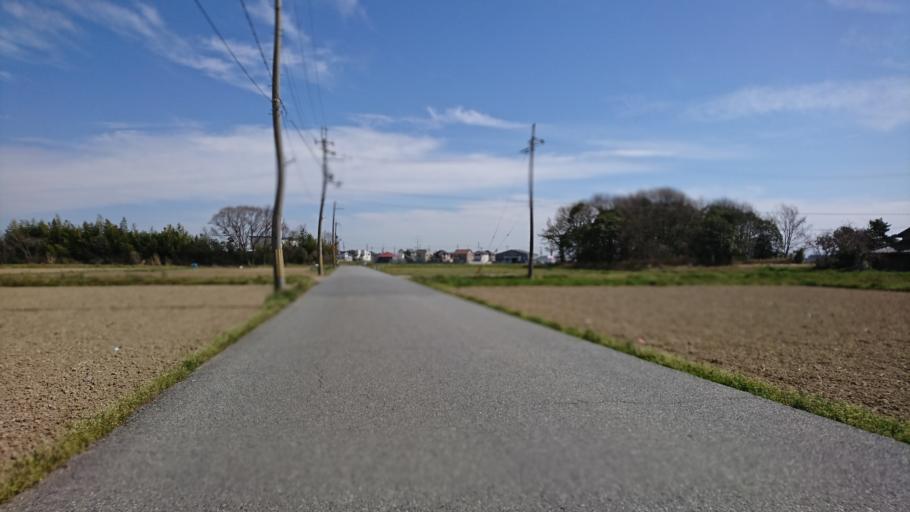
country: JP
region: Hyogo
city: Miki
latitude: 34.7650
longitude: 134.9320
